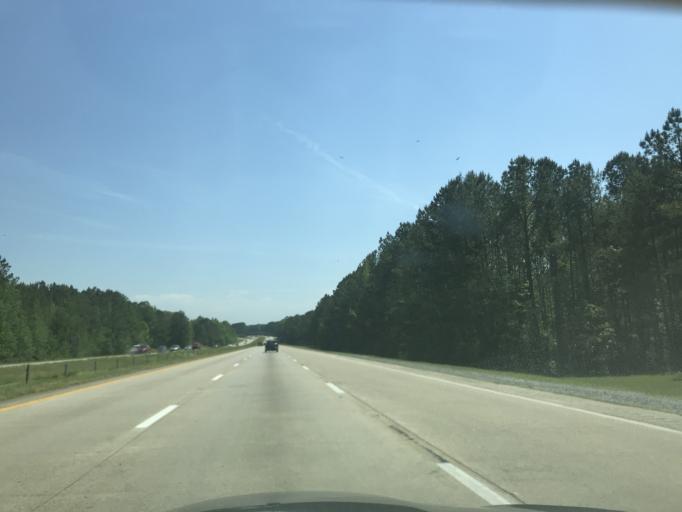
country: US
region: North Carolina
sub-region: Johnston County
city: Benson
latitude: 35.4331
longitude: -78.5329
